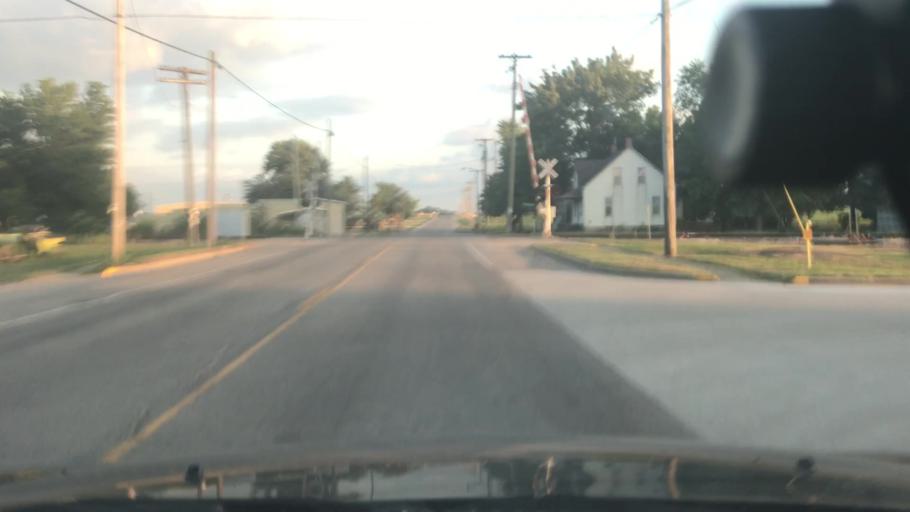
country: US
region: Illinois
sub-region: Washington County
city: Okawville
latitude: 38.4227
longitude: -89.5506
